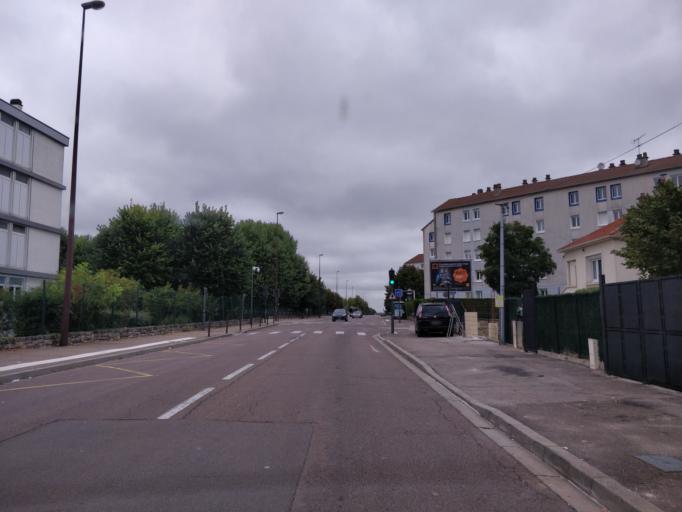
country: FR
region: Champagne-Ardenne
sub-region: Departement de l'Aube
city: Rosieres-pres-Troyes
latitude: 48.2745
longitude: 4.0733
